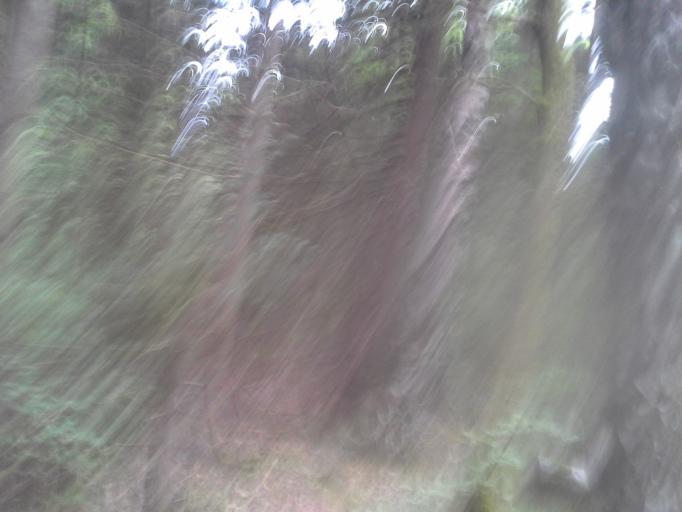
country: RU
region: Moskovskaya
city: Kievskij
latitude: 55.4445
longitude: 36.8537
